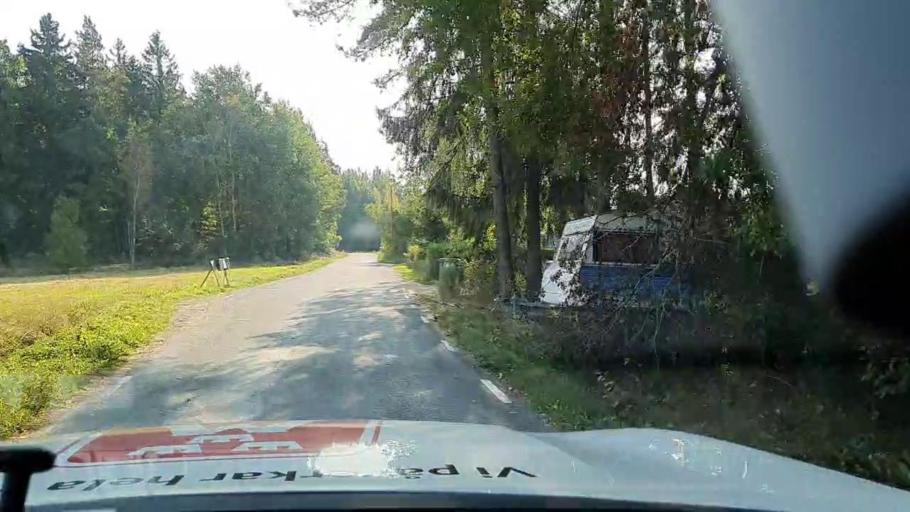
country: SE
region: Soedermanland
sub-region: Eskilstuna Kommun
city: Kvicksund
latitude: 59.3218
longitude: 16.2435
